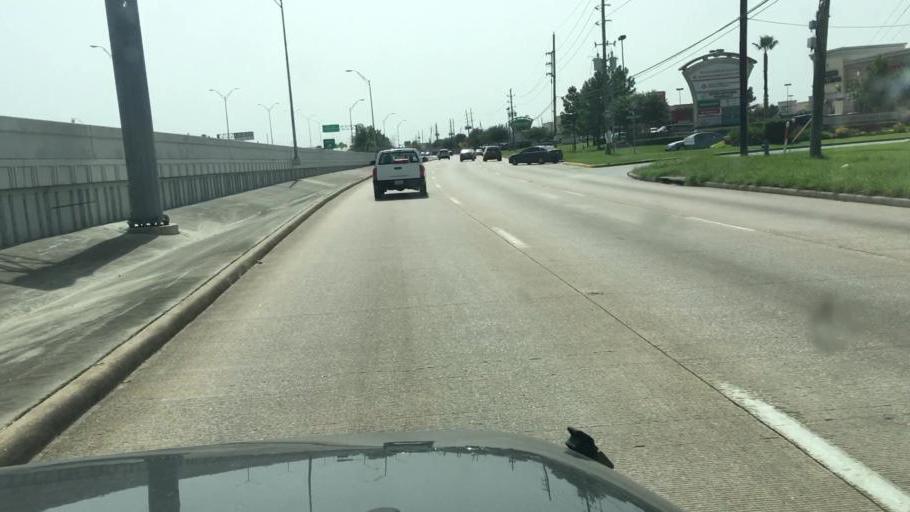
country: US
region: Texas
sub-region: Harris County
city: Humble
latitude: 29.9351
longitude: -95.2439
